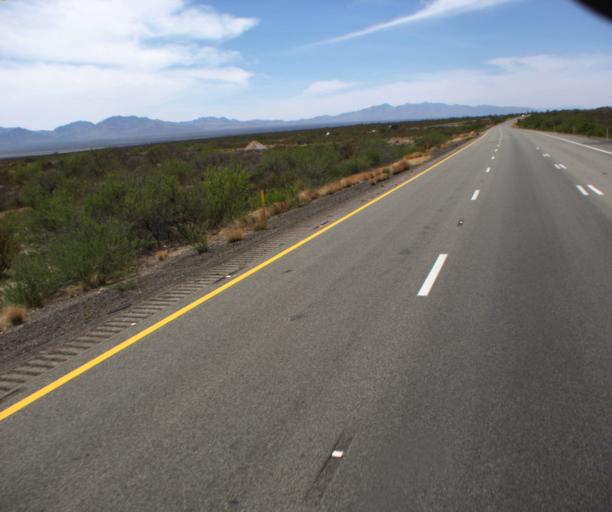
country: US
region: New Mexico
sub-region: Hidalgo County
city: Lordsburg
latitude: 32.2390
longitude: -109.0920
